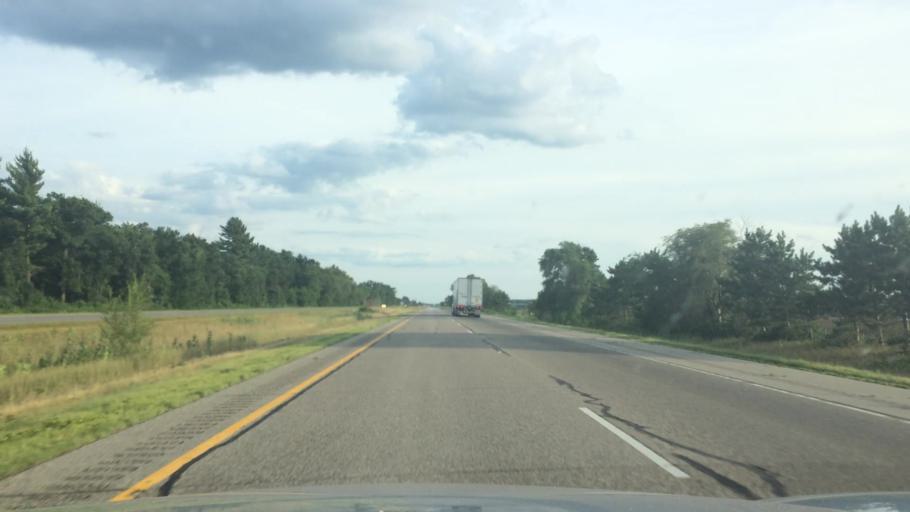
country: US
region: Wisconsin
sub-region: Portage County
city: Plover
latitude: 44.2509
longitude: -89.5242
